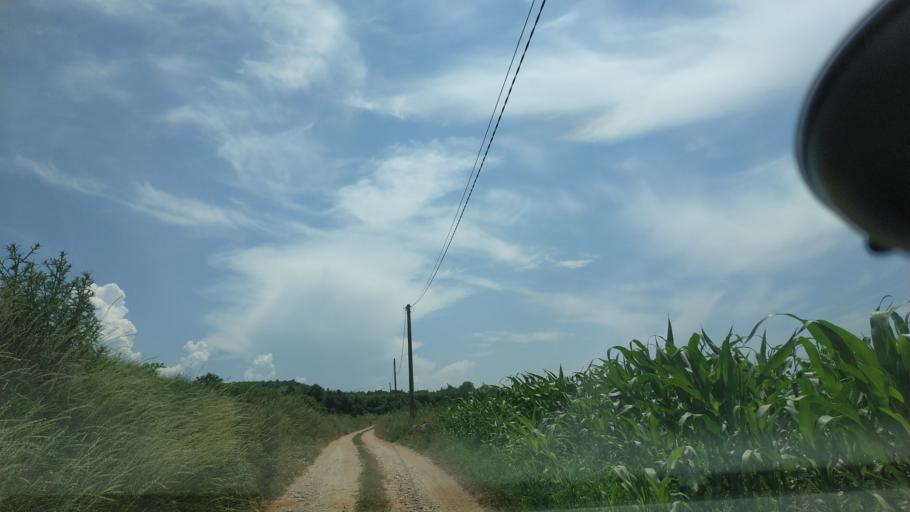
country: RS
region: Central Serbia
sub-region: Nisavski Okrug
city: Aleksinac
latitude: 43.5720
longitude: 21.7047
